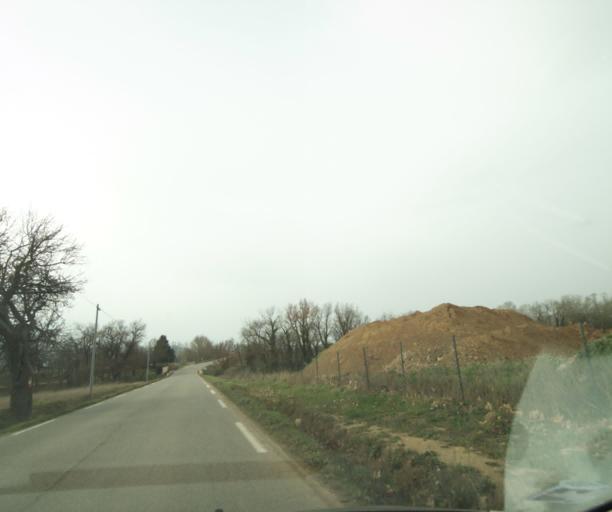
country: FR
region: Provence-Alpes-Cote d'Azur
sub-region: Departement du Var
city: Pourrieres
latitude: 43.4807
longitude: 5.7174
